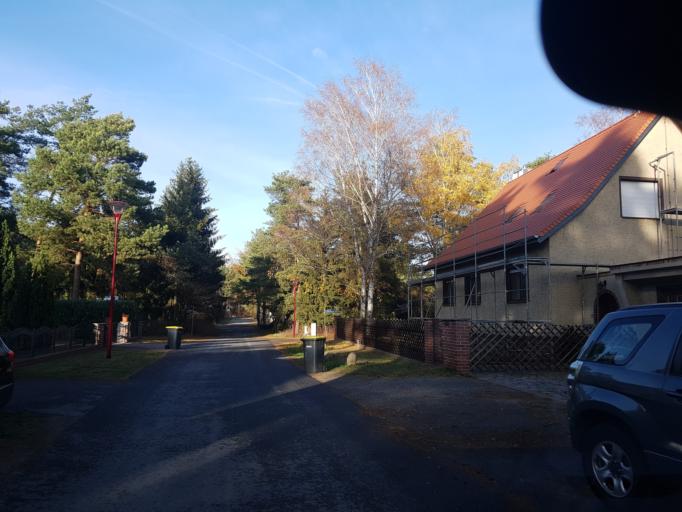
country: DE
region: Brandenburg
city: Finsterwalde
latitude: 51.6409
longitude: 13.6737
